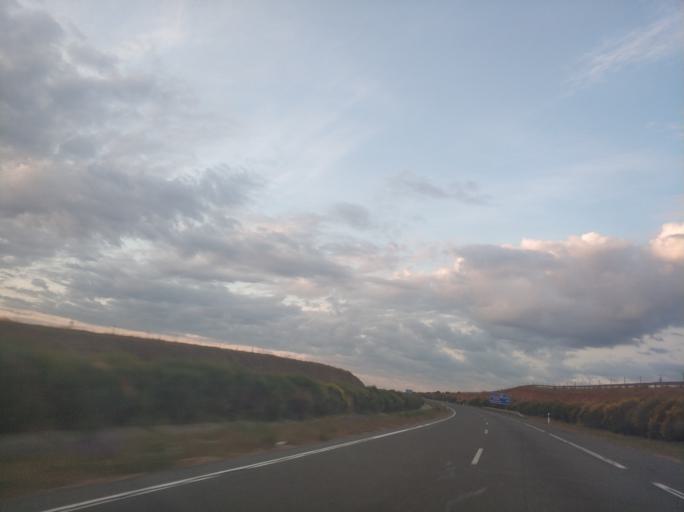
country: ES
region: Castille and Leon
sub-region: Provincia de Salamanca
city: Miranda de Azan
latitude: 40.8789
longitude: -5.6672
